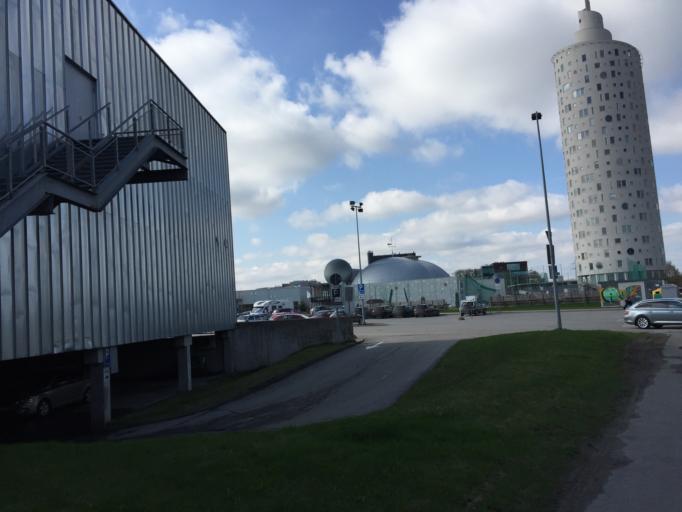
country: EE
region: Tartu
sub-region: Tartu linn
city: Tartu
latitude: 58.3750
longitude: 26.7369
